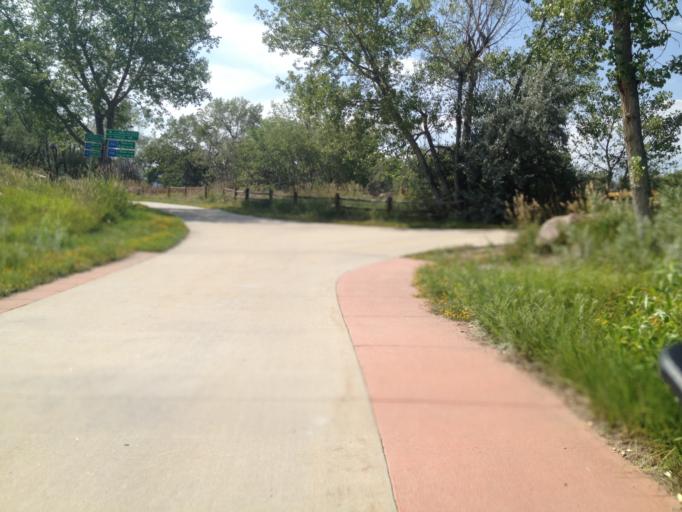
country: US
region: Colorado
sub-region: Boulder County
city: Boulder
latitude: 40.0262
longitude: -105.2217
